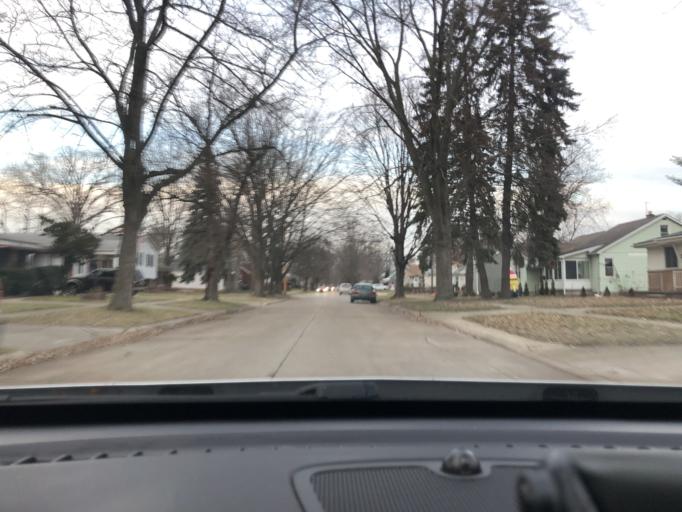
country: US
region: Michigan
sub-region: Wayne County
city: Allen Park
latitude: 42.2782
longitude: -83.2363
